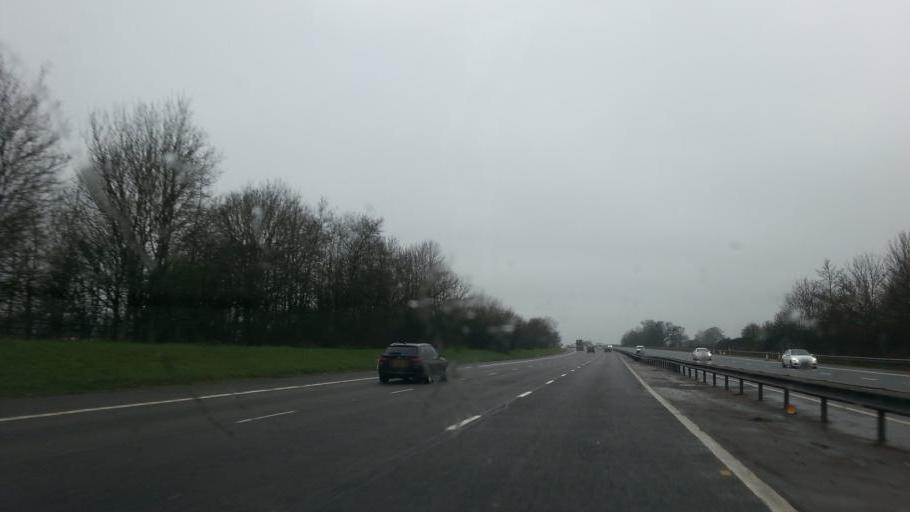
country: GB
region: England
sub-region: Oxfordshire
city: Hanwell
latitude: 52.1451
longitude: -1.4153
